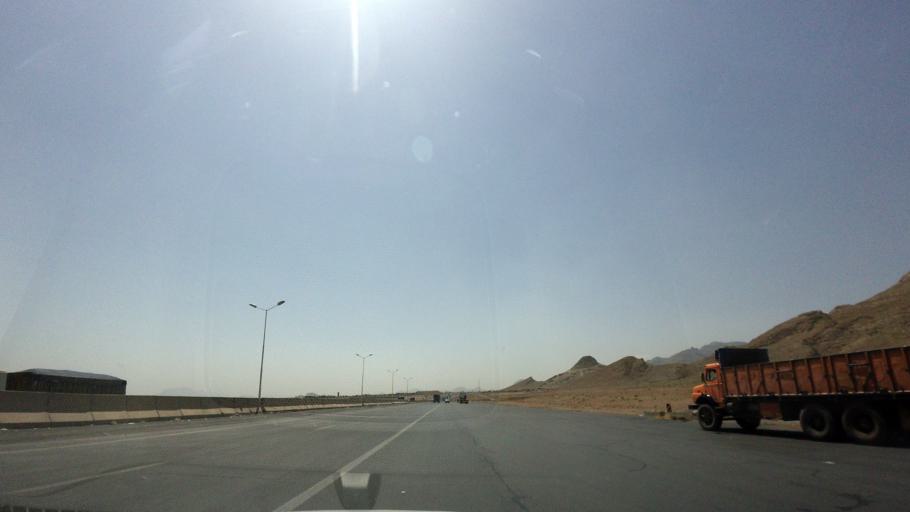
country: IR
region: Isfahan
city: Najafabad
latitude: 32.5816
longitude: 51.2888
